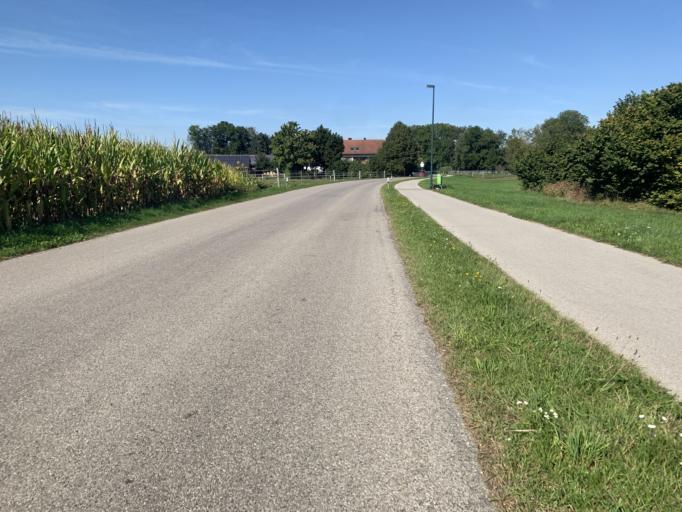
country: DE
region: Bavaria
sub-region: Swabia
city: Kissing
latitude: 48.3110
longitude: 10.9817
